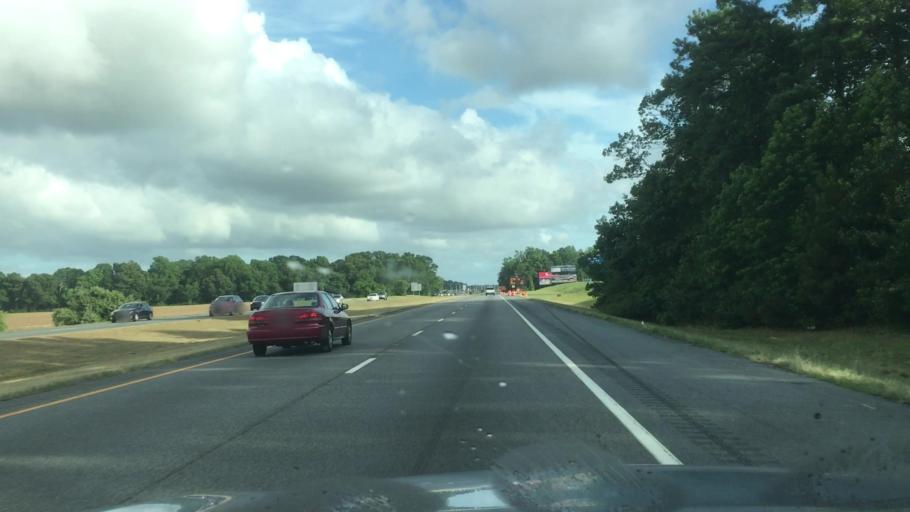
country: US
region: Delaware
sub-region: Kent County
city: Riverview
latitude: 39.0051
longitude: -75.4568
